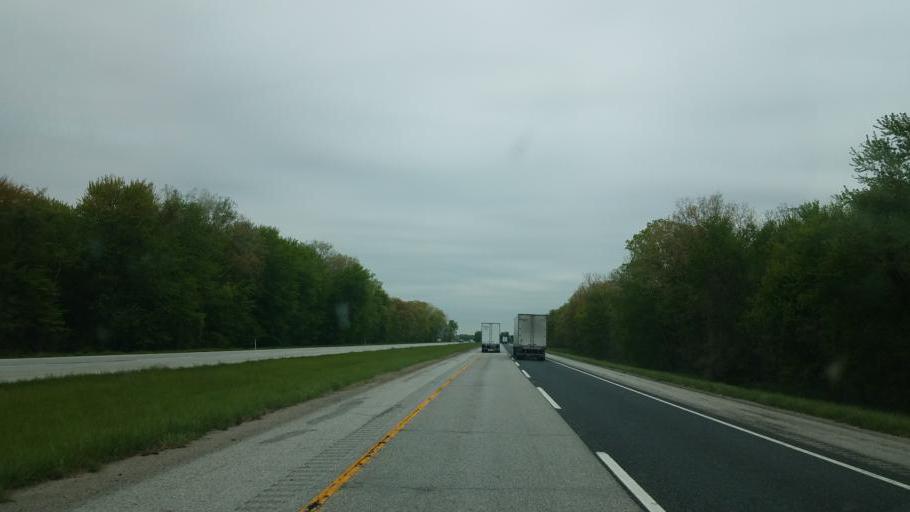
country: US
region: Michigan
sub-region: Saint Joseph County
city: Sturgis
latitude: 41.7533
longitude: -85.4644
